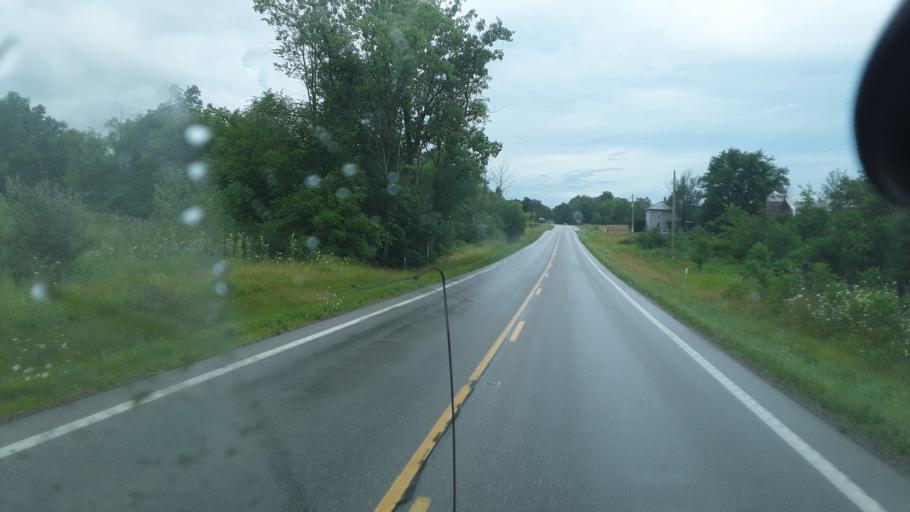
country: US
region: Indiana
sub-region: Steuben County
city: Hamilton
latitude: 41.6322
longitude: -84.7983
